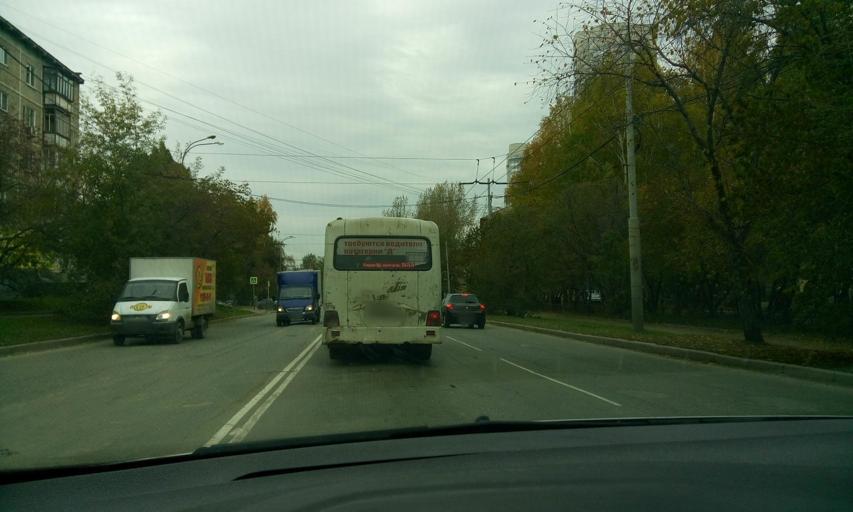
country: RU
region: Sverdlovsk
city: Yekaterinburg
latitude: 56.8599
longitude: 60.6535
